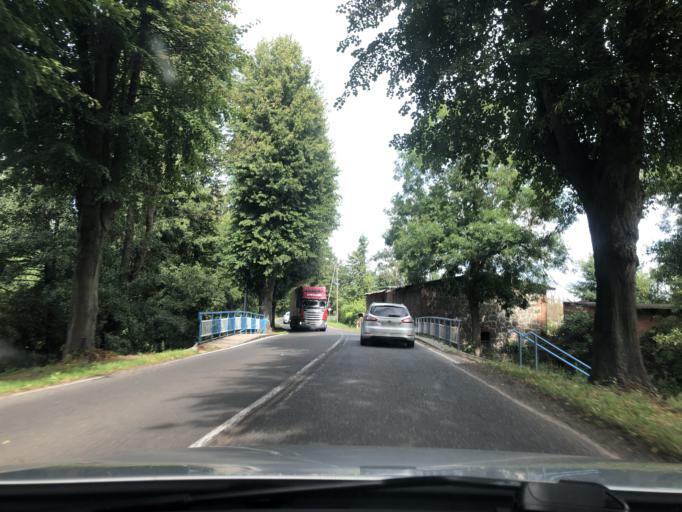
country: PL
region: Greater Poland Voivodeship
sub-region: Powiat pilski
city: Szydlowo
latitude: 53.0934
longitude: 16.6326
